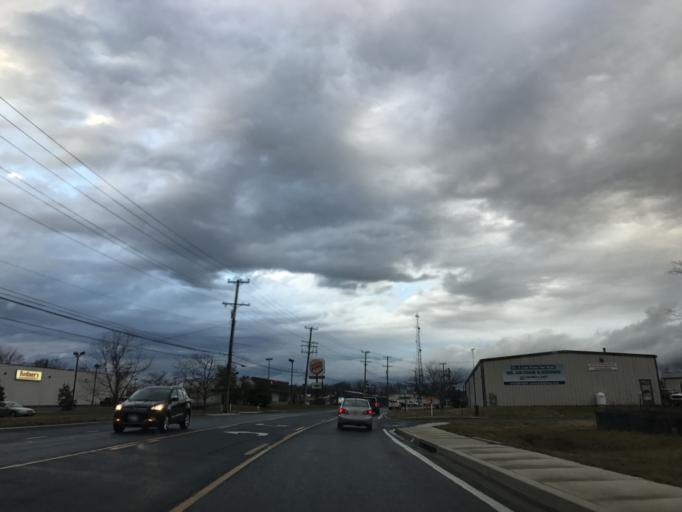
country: US
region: Maryland
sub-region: Harford County
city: Bel Air North
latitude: 39.5763
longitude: -76.3438
